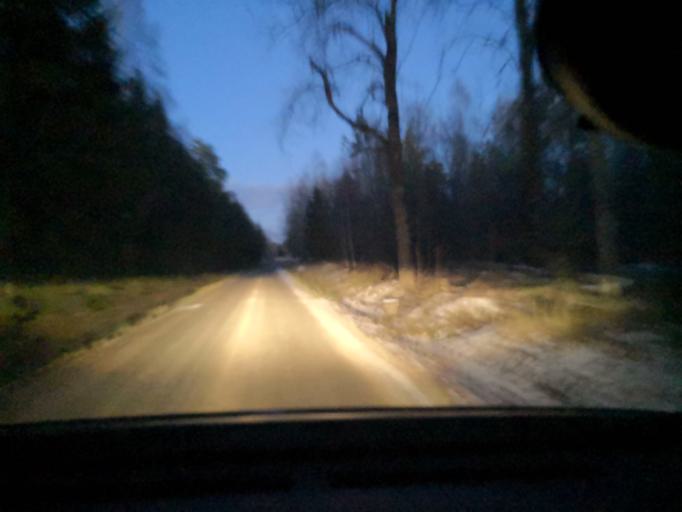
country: SE
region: Vaestmanland
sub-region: Sala Kommun
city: Sala
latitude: 59.8771
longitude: 16.7301
